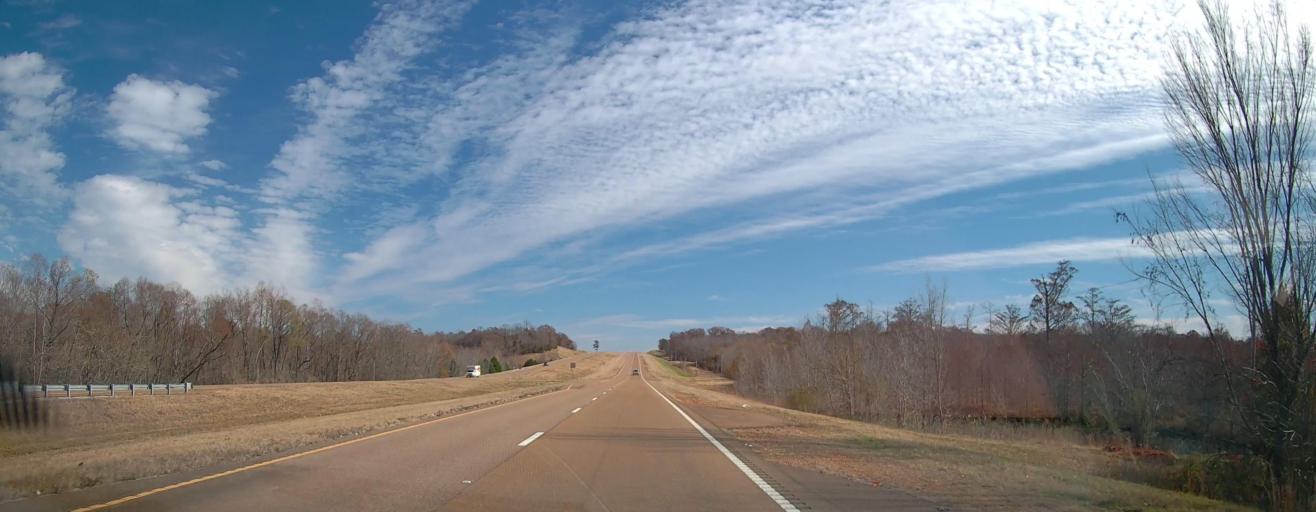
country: US
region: Mississippi
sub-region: Benton County
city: Ashland
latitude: 34.9460
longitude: -89.1952
